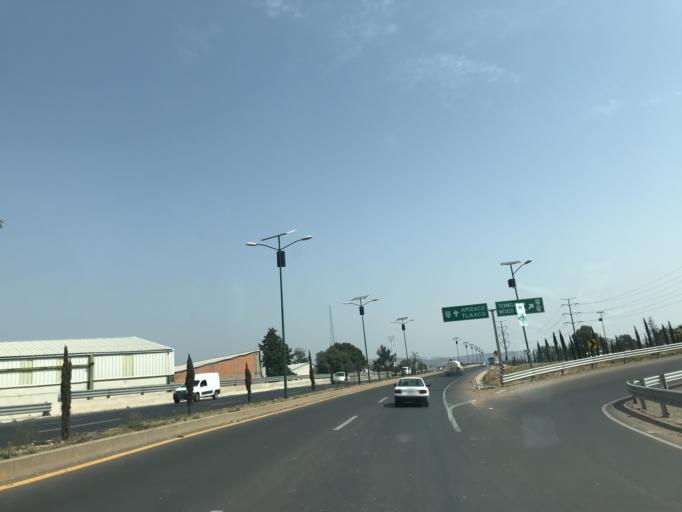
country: MX
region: Tlaxcala
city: Tlaxcala de Xicohtencatl
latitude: 19.3049
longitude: -98.1996
